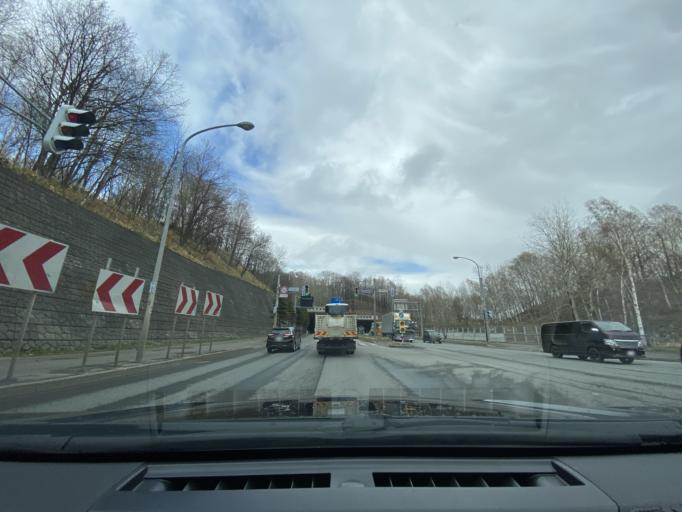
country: JP
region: Hokkaido
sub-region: Asahikawa-shi
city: Asahikawa
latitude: 43.8012
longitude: 142.3425
